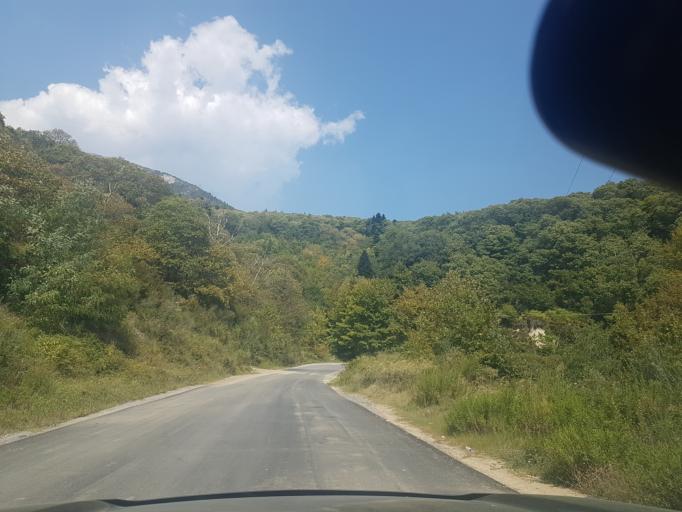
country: GR
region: Central Greece
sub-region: Nomos Evvoias
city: Yimnon
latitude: 38.6260
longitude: 23.8939
